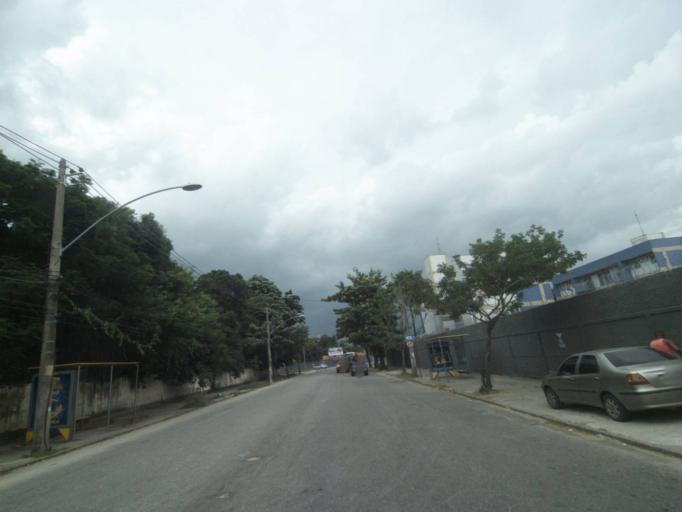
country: BR
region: Rio de Janeiro
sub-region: Nilopolis
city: Nilopolis
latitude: -22.8861
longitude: -43.3899
